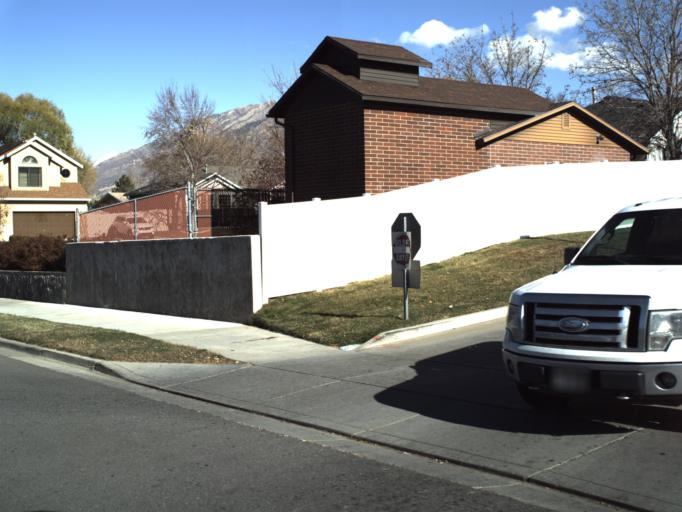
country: US
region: Utah
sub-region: Salt Lake County
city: Sandy Hills
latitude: 40.5833
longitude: -111.8339
